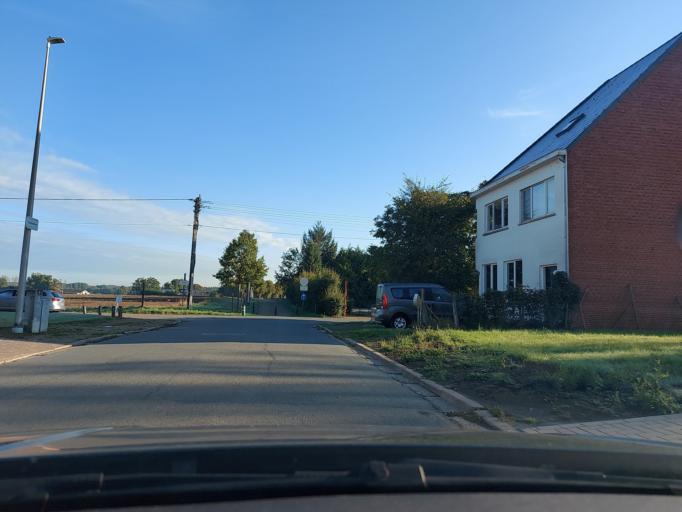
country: BE
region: Flanders
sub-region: Provincie Limburg
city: Hasselt
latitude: 50.9450
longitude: 5.2948
